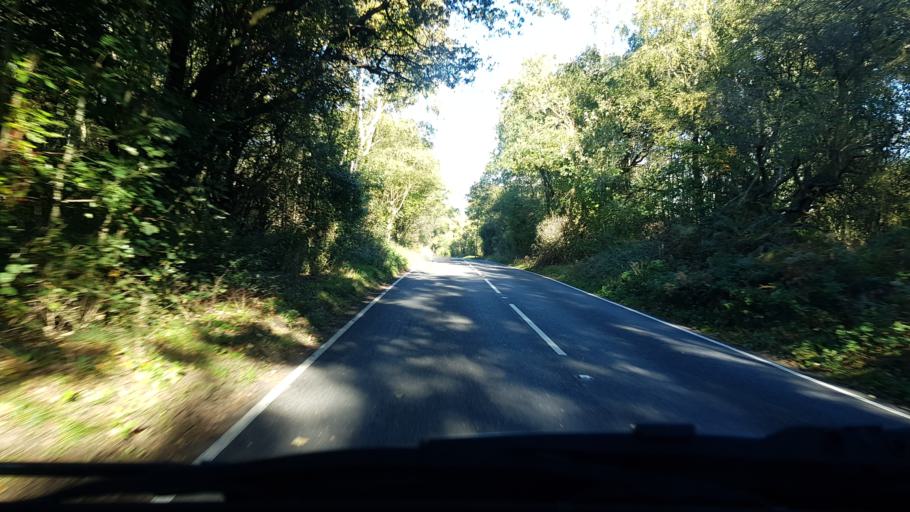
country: GB
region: England
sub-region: Surrey
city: Chilworth
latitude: 51.2382
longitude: -0.5060
